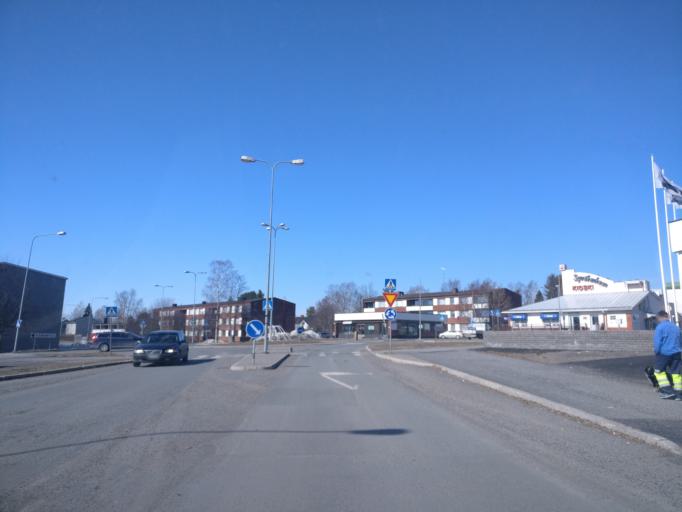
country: FI
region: Lapland
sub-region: Kemi-Tornio
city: Kemi
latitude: 65.7295
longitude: 24.6031
